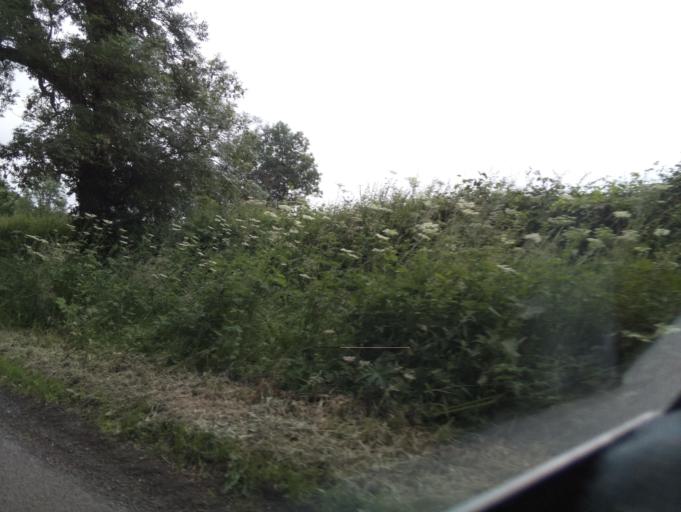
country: GB
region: England
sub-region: Leicestershire
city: Melton Mowbray
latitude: 52.7123
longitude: -0.8320
